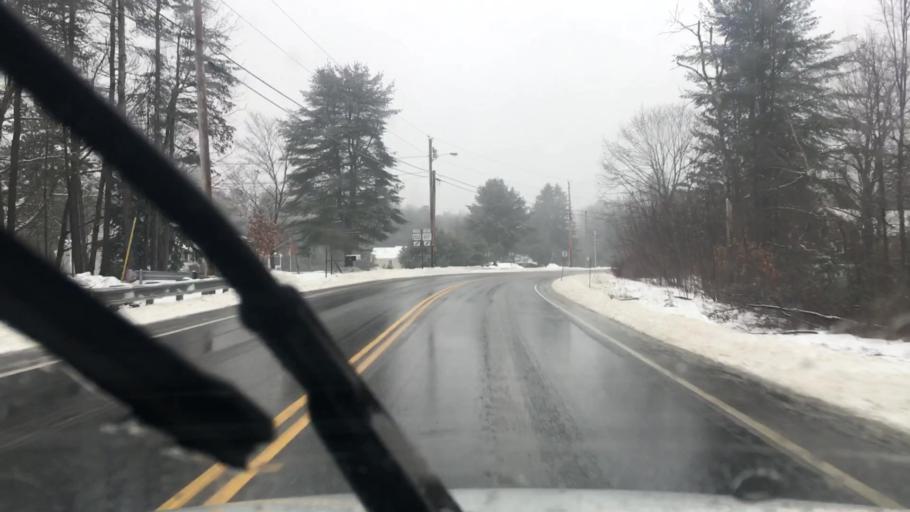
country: US
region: Maine
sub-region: York County
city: Buxton
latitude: 43.5977
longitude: -70.5336
